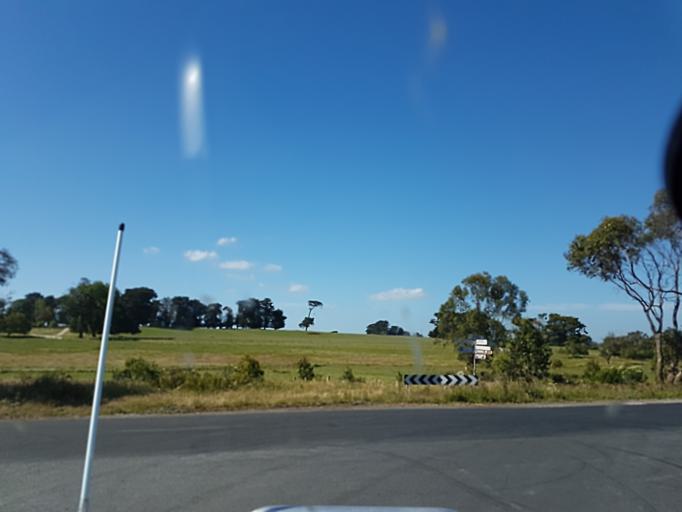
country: AU
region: Victoria
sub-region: Bass Coast
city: North Wonthaggi
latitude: -38.5664
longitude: 145.8993
